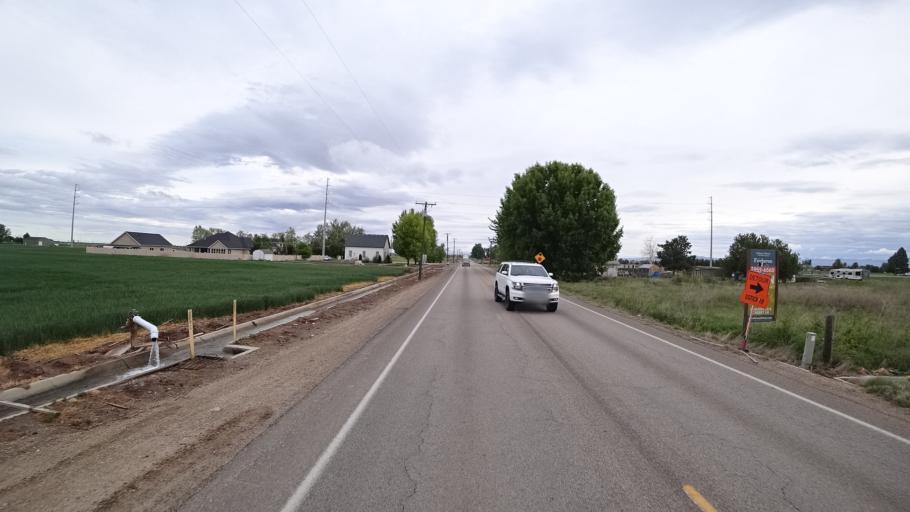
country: US
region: Idaho
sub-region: Ada County
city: Star
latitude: 43.6473
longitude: -116.4936
